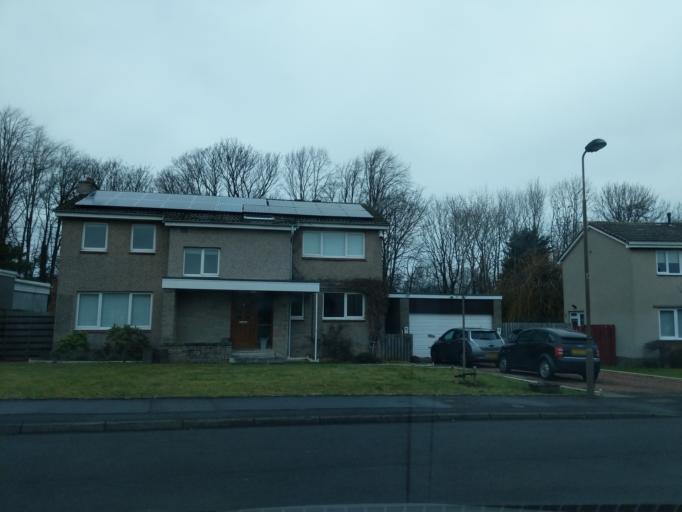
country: GB
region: Scotland
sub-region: Edinburgh
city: Balerno
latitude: 55.8926
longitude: -3.3303
